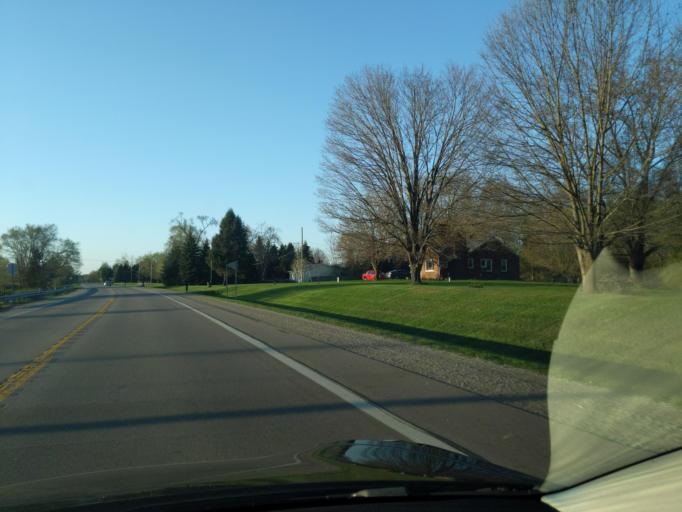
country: US
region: Michigan
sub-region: Ingham County
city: Stockbridge
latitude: 42.4266
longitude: -84.1728
